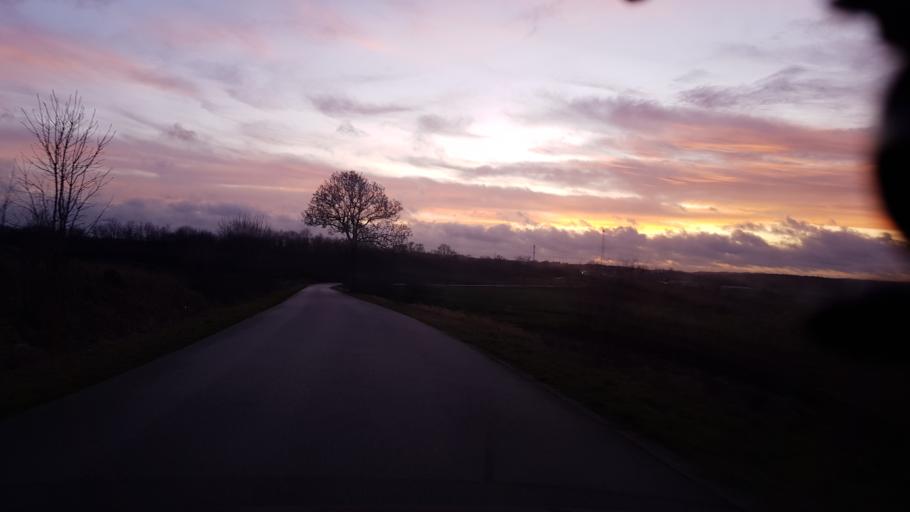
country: PL
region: Pomeranian Voivodeship
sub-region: Powiat bytowski
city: Tuchomie
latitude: 54.1283
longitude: 17.3503
